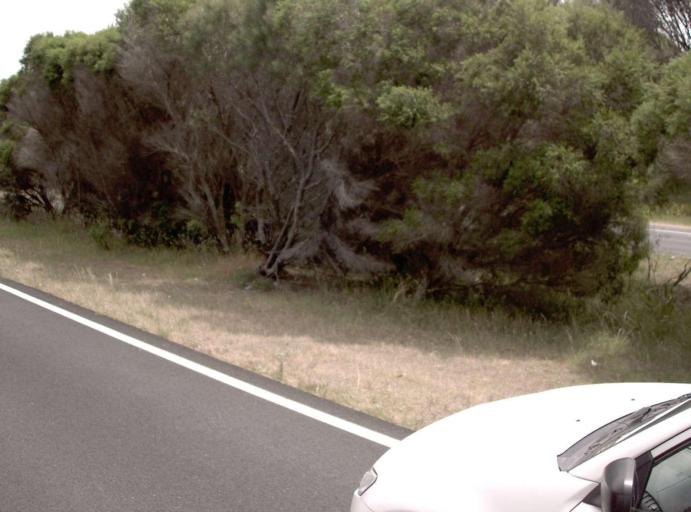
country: AU
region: Victoria
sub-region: Mornington Peninsula
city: McCrae
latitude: -38.3475
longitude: 144.9407
